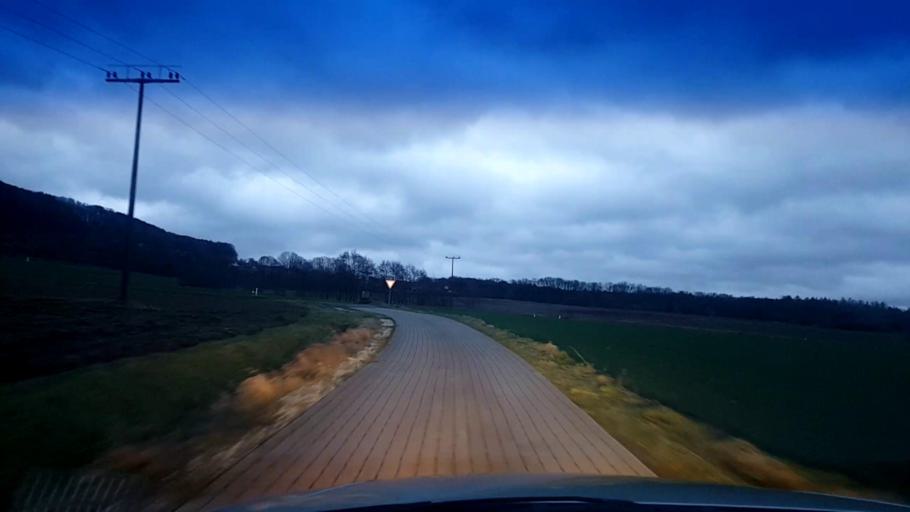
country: DE
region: Bavaria
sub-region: Upper Franconia
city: Schesslitz
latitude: 49.9904
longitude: 11.0506
